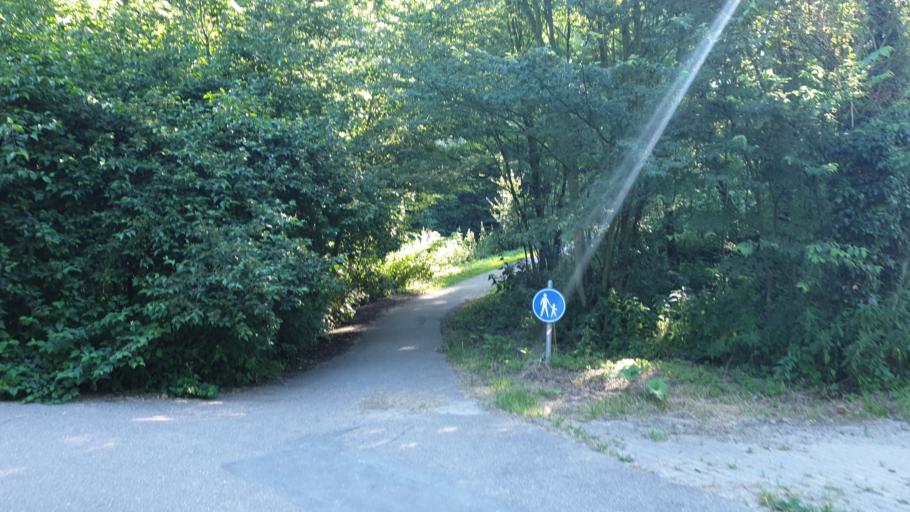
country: NL
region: South Holland
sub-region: Gemeente Westland
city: Poeldijk
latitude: 52.0541
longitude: 4.2174
